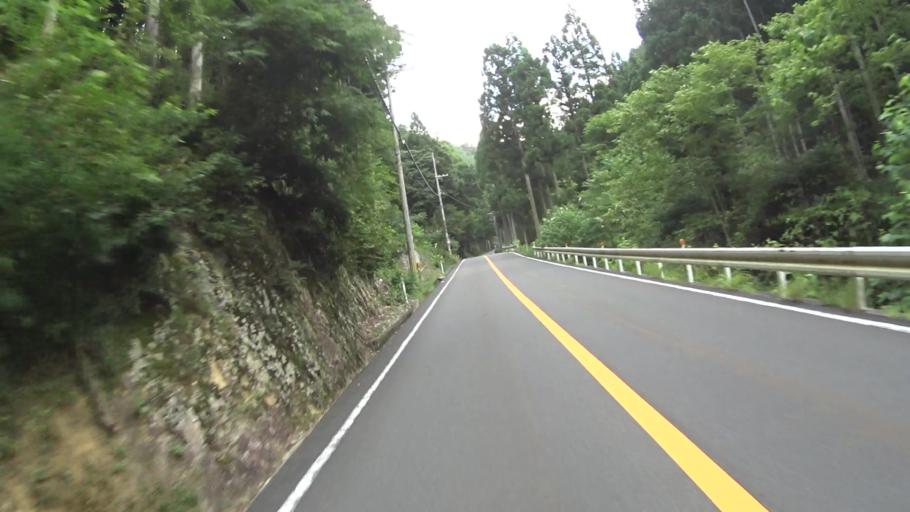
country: JP
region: Kyoto
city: Kameoka
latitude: 35.2575
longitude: 135.6150
